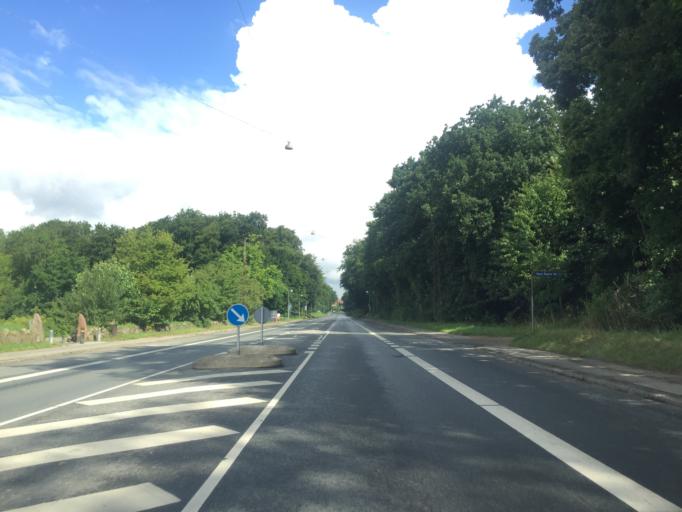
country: DK
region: South Denmark
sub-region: Odense Kommune
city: Odense
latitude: 55.3663
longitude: 10.3861
